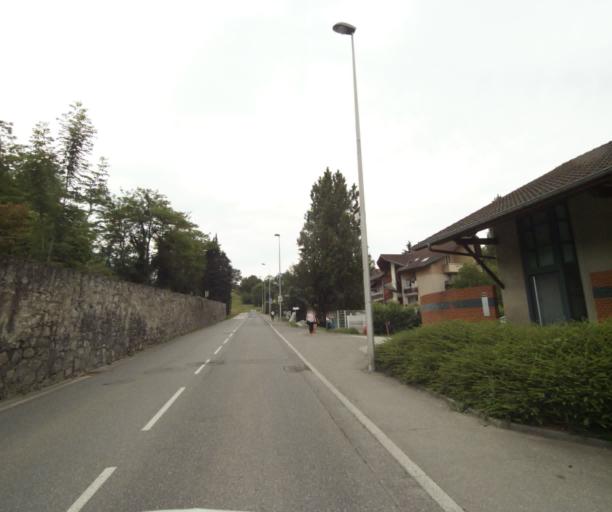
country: FR
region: Rhone-Alpes
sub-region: Departement de la Haute-Savoie
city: Thonon-les-Bains
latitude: 46.3579
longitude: 6.4781
